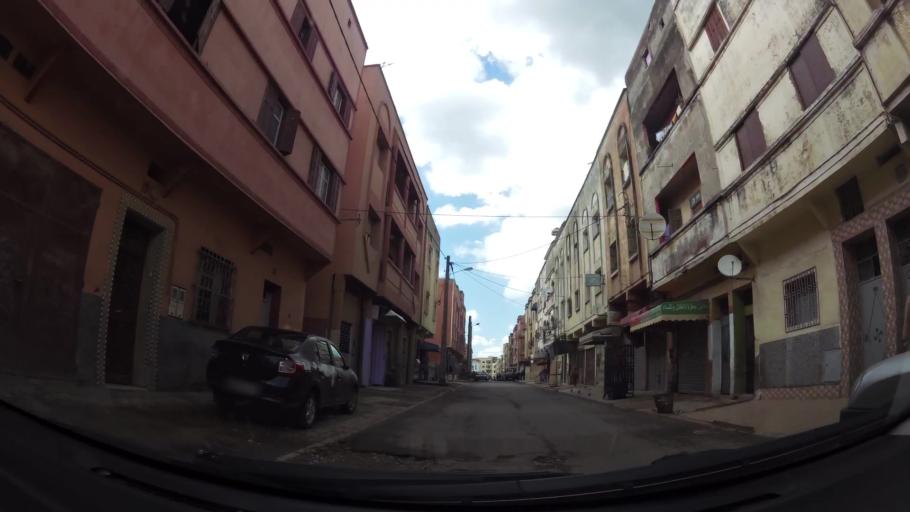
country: MA
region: Chaouia-Ouardigha
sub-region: Settat Province
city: Berrechid
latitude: 33.2712
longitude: -7.5887
